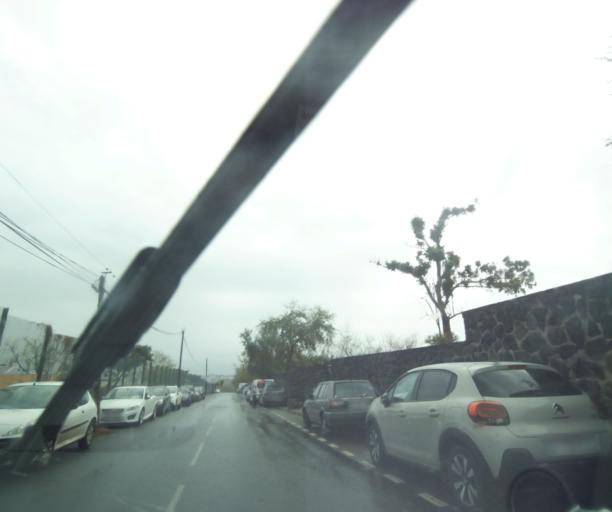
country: RE
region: Reunion
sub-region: Reunion
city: Le Port
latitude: -20.9747
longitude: 55.3017
